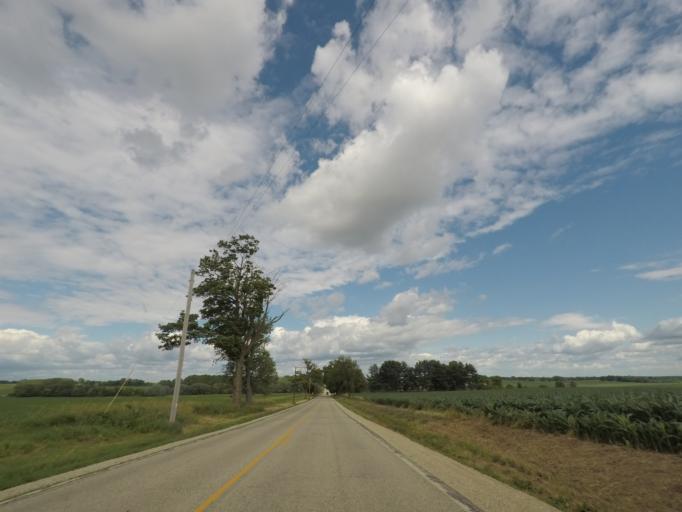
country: US
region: Wisconsin
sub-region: Rock County
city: Orfordville
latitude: 42.7111
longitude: -89.1999
